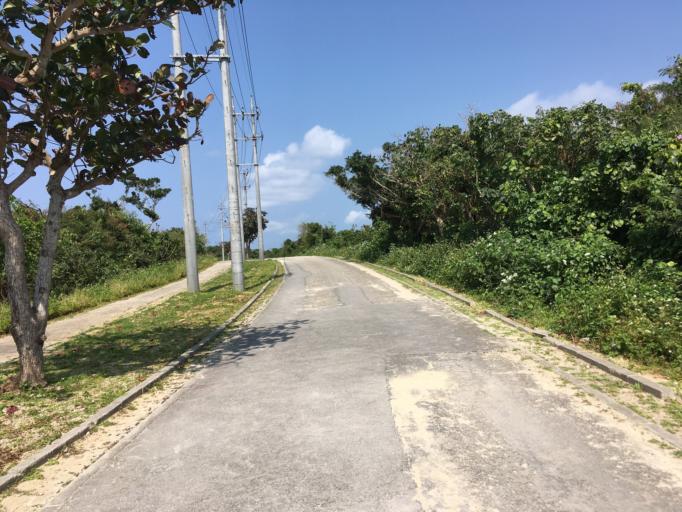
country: JP
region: Okinawa
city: Ishigaki
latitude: 24.3285
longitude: 124.0800
